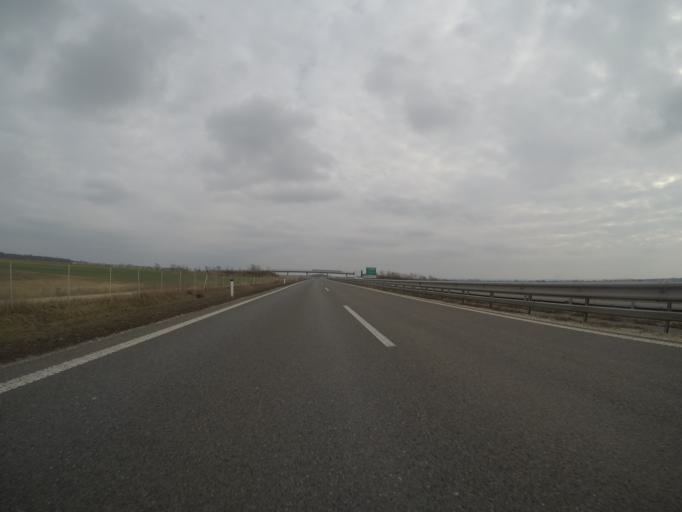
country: SI
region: Turnisce
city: Turnisce
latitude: 46.6296
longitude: 16.2865
